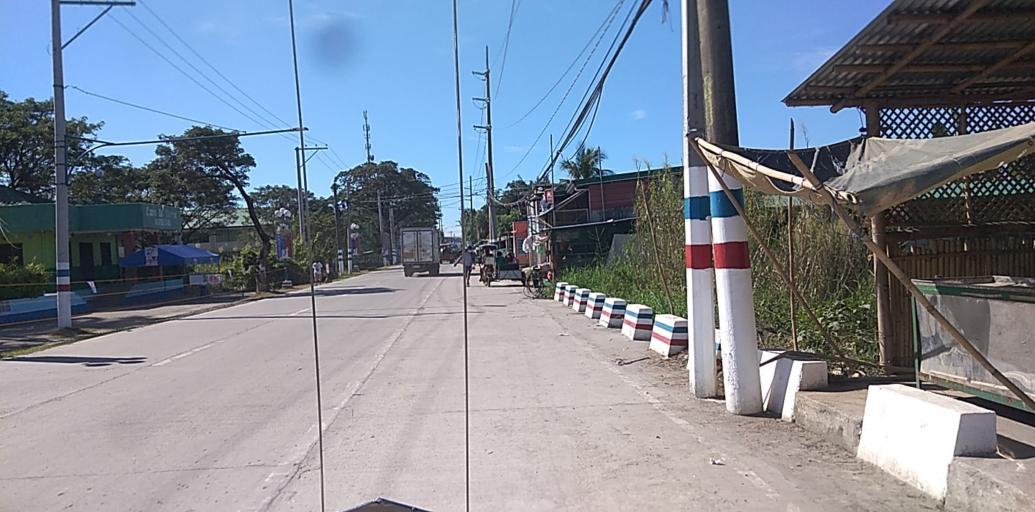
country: PH
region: Central Luzon
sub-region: Province of Pampanga
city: San Luis
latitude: 15.0426
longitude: 120.7895
